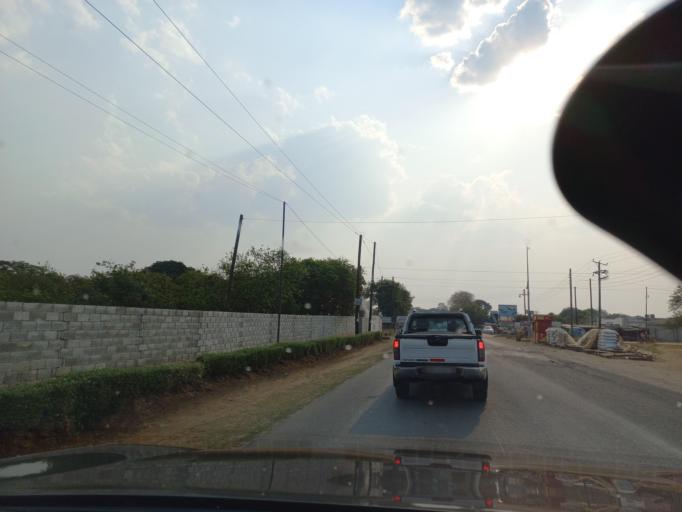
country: ZM
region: Lusaka
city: Lusaka
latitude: -15.4639
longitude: 28.2377
